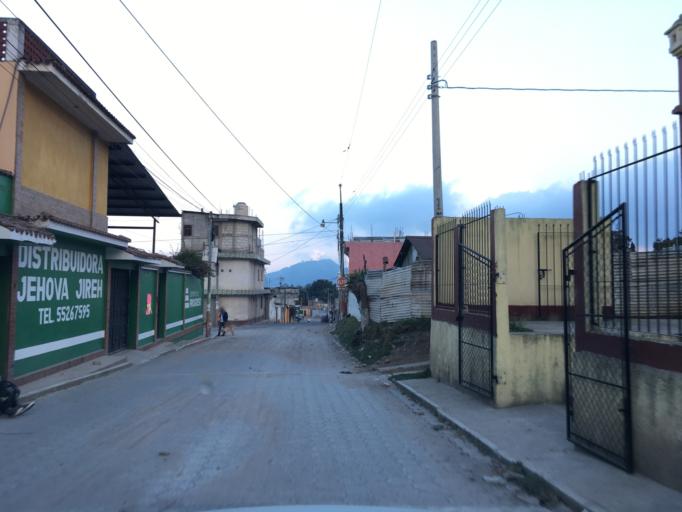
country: GT
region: Chimaltenango
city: Tecpan Guatemala
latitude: 14.7583
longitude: -91.0009
